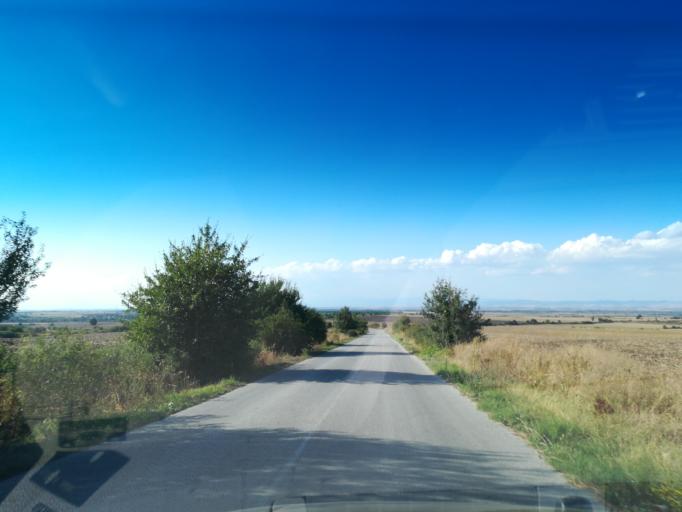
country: BG
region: Khaskovo
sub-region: Obshtina Mineralni Bani
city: Mineralni Bani
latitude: 42.0422
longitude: 25.2818
